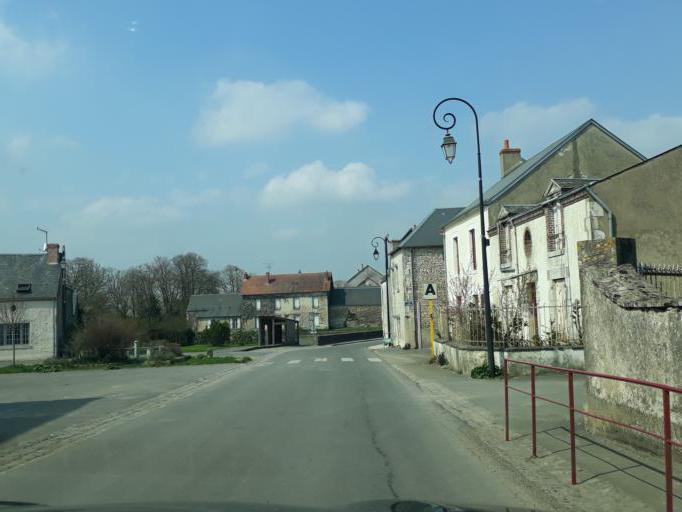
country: FR
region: Centre
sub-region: Departement d'Eure-et-Loir
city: Baigneaux
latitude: 48.0995
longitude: 1.8399
